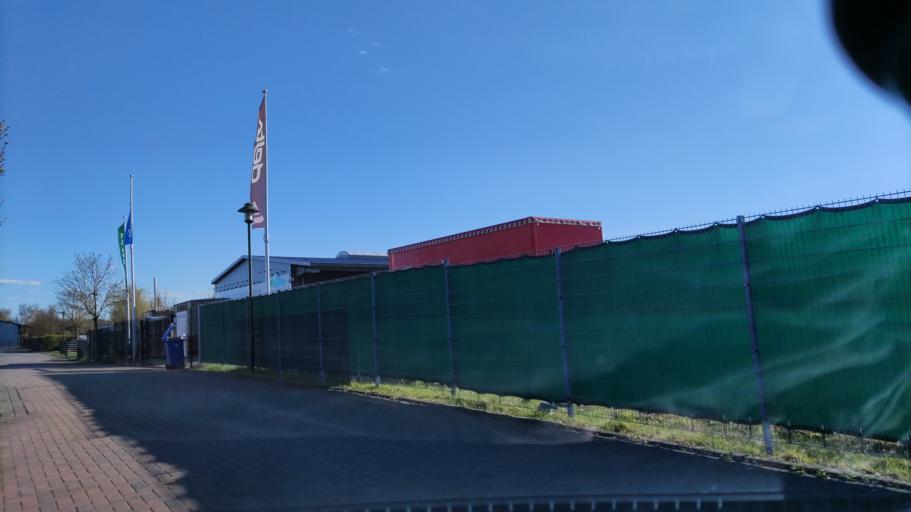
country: DE
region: Lower Saxony
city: Hanstedt
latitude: 53.2739
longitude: 10.0055
